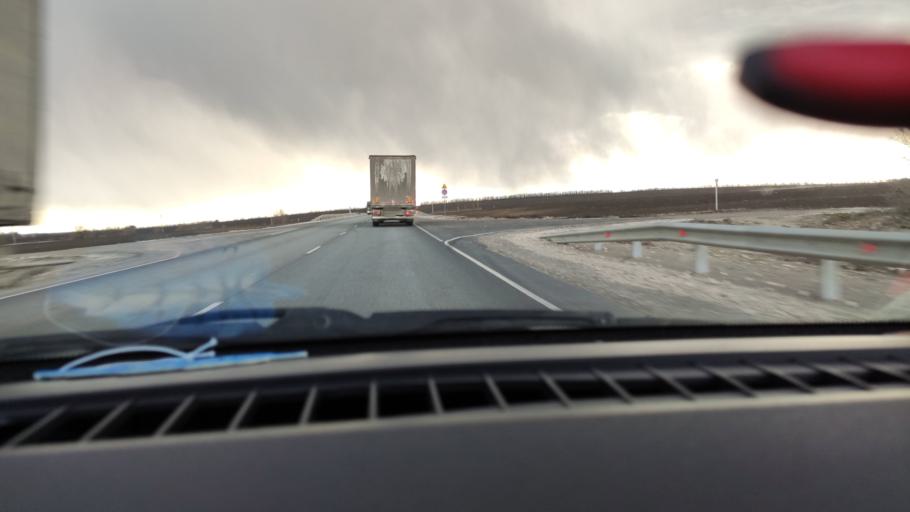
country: RU
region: Saratov
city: Yelshanka
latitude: 51.8440
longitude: 46.4811
